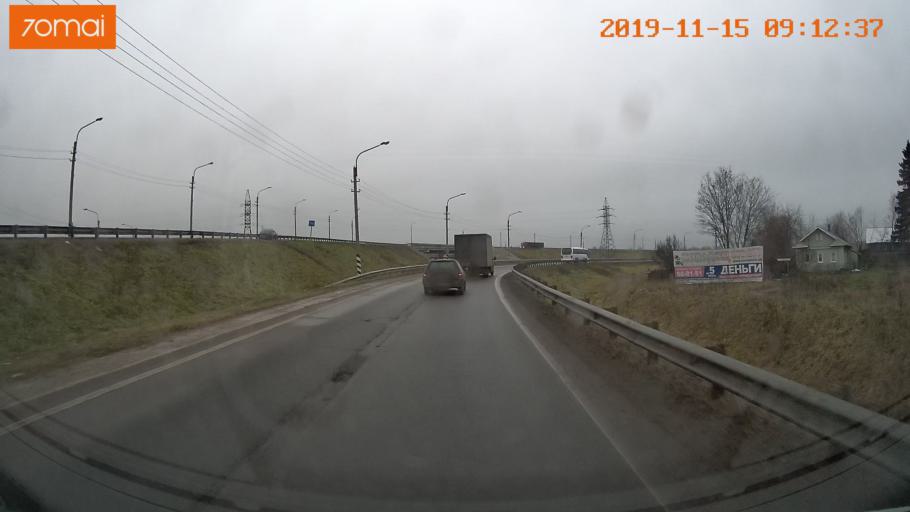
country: RU
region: Vologda
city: Tonshalovo
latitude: 59.2097
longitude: 37.9359
